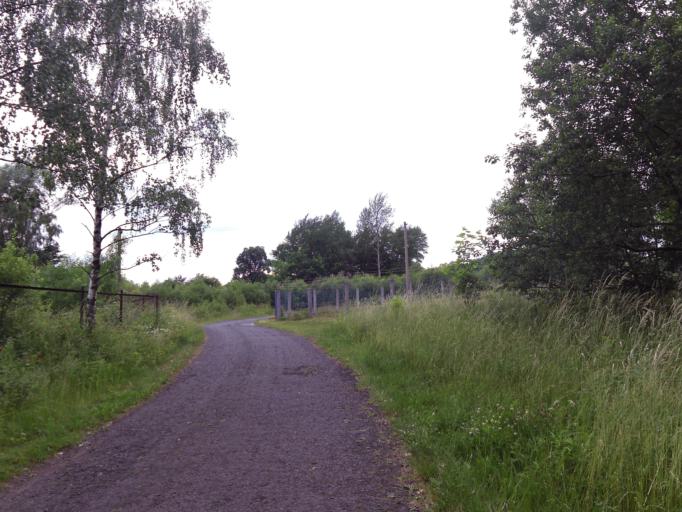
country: CZ
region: Ustecky
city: Dolni Podluzi
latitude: 50.8825
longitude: 14.6201
